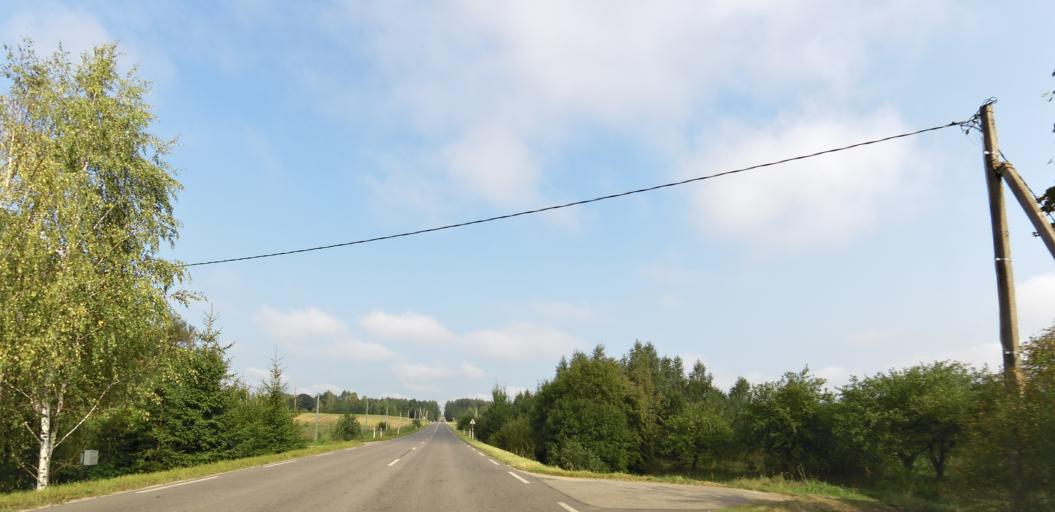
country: LT
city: Grigiskes
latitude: 54.7633
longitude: 25.0807
